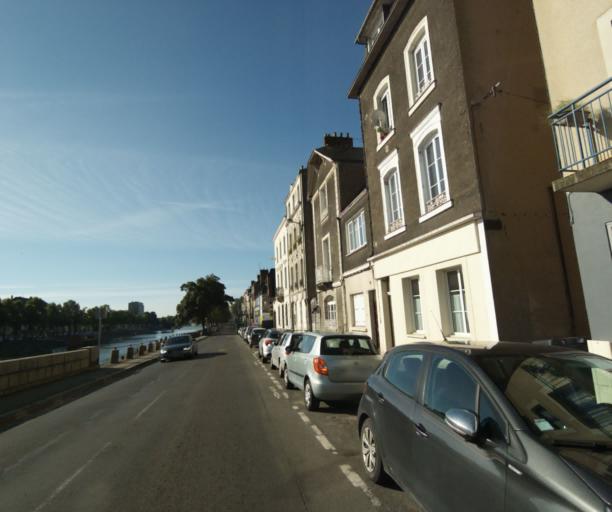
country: FR
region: Pays de la Loire
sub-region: Departement de la Mayenne
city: Laval
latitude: 48.0676
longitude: -0.7695
